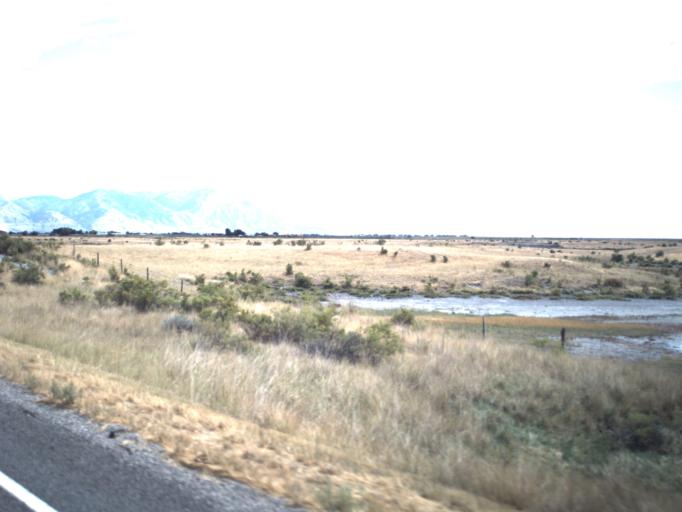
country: US
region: Utah
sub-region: Box Elder County
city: Elwood
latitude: 41.5777
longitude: -112.2393
